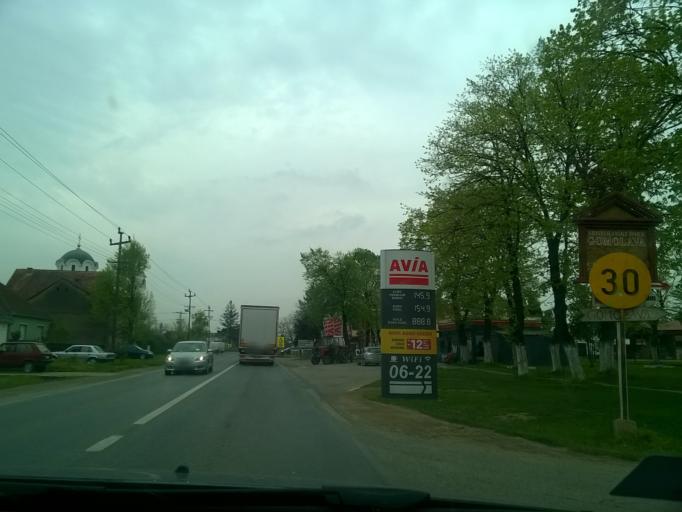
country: RS
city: Hrtkovci
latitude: 44.8823
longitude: 19.7631
